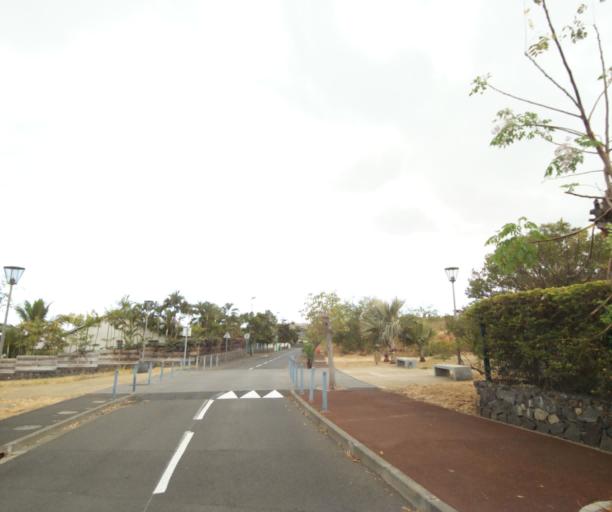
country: RE
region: Reunion
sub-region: Reunion
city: Saint-Paul
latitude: -21.0624
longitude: 55.2256
